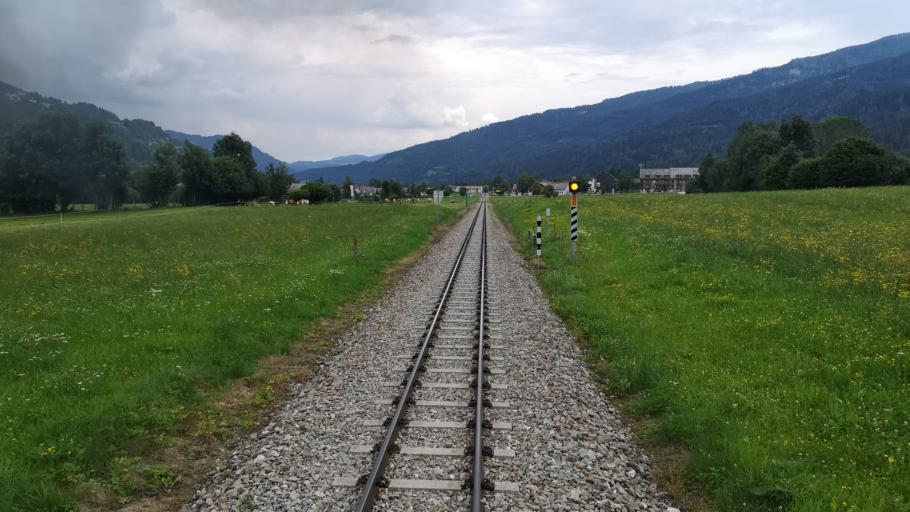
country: AT
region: Styria
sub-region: Politischer Bezirk Murau
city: Sankt Georgen ob Murau
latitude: 47.1024
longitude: 14.0820
